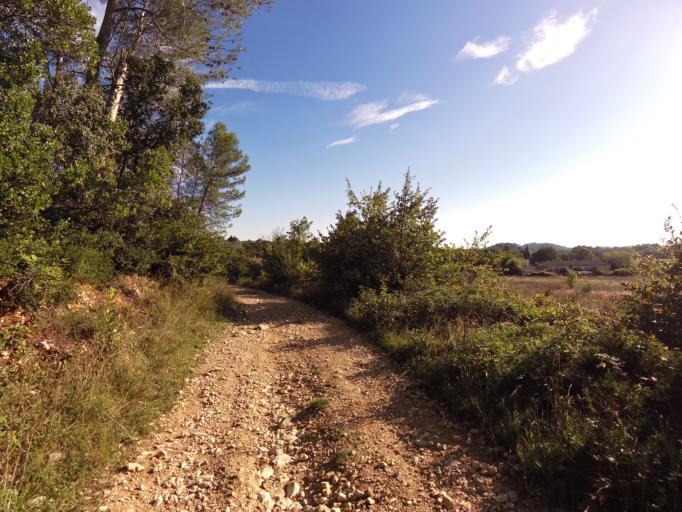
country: FR
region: Languedoc-Roussillon
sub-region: Departement du Gard
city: Villevieille
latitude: 43.8120
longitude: 4.0872
